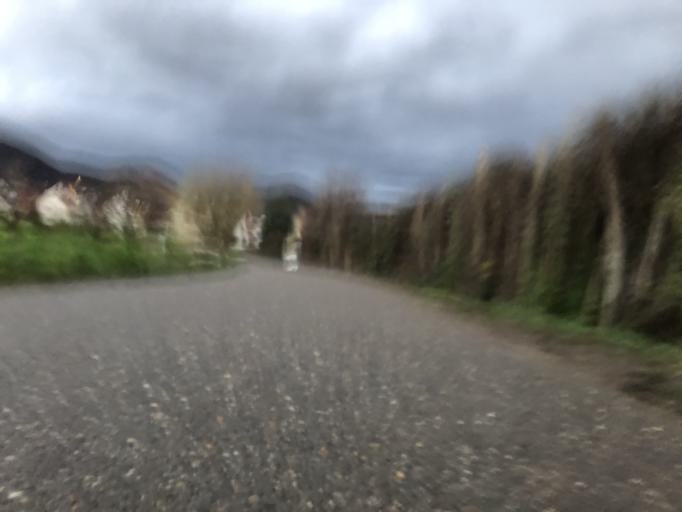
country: DE
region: Baden-Wuerttemberg
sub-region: Karlsruhe Region
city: Dossenheim
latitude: 49.4450
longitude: 8.6633
